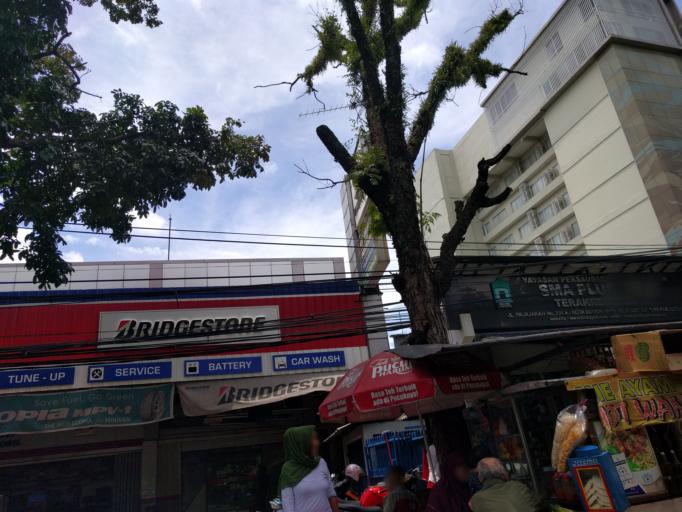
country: ID
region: West Java
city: Bogor
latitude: -6.5781
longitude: 106.8074
